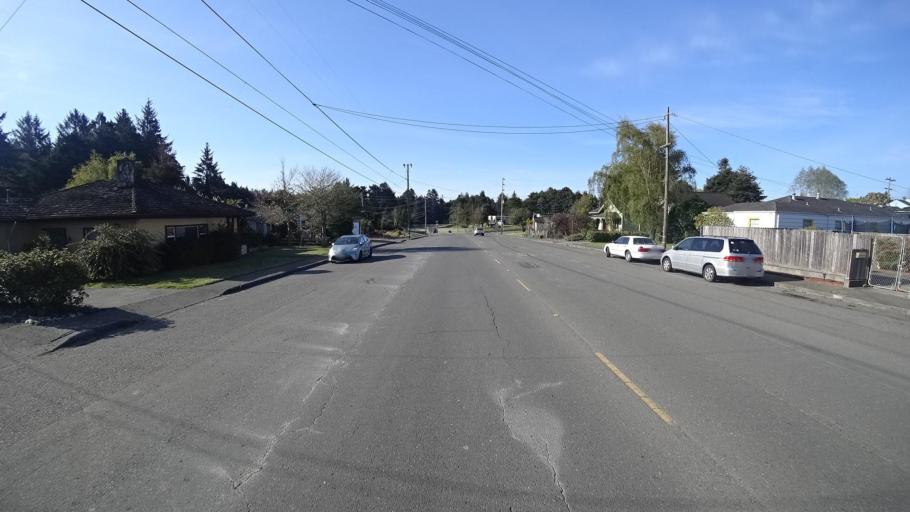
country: US
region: California
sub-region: Humboldt County
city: Cutten
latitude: 40.7722
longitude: -124.1614
